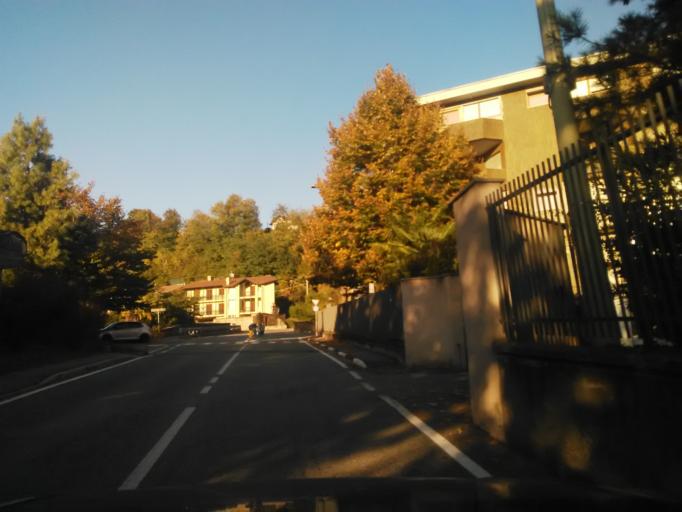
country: IT
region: Piedmont
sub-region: Provincia di Vercelli
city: Borgosesia
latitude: 45.7129
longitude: 8.2883
